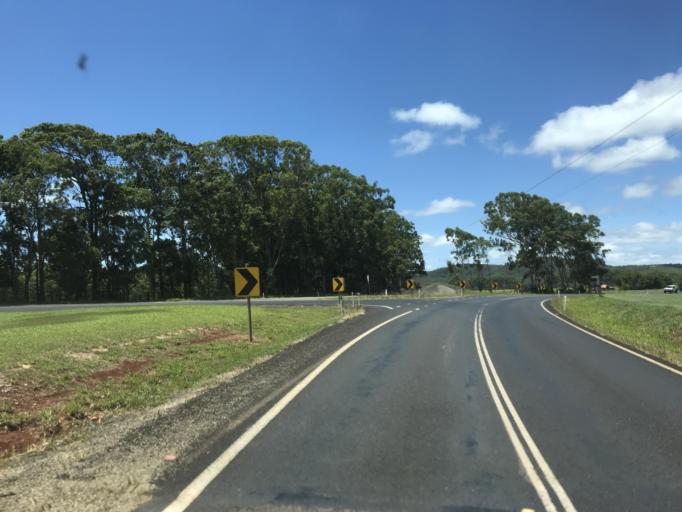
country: AU
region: Queensland
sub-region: Tablelands
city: Ravenshoe
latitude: -17.5150
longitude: 145.4504
